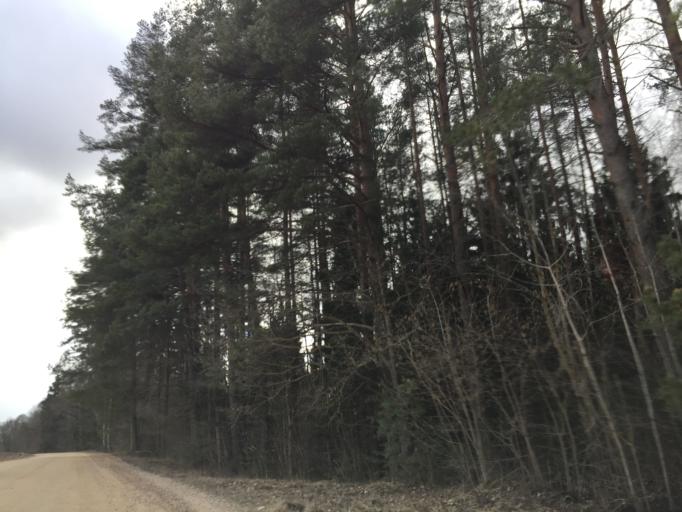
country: LV
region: Akniste
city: Akniste
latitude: 56.1085
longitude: 25.8288
